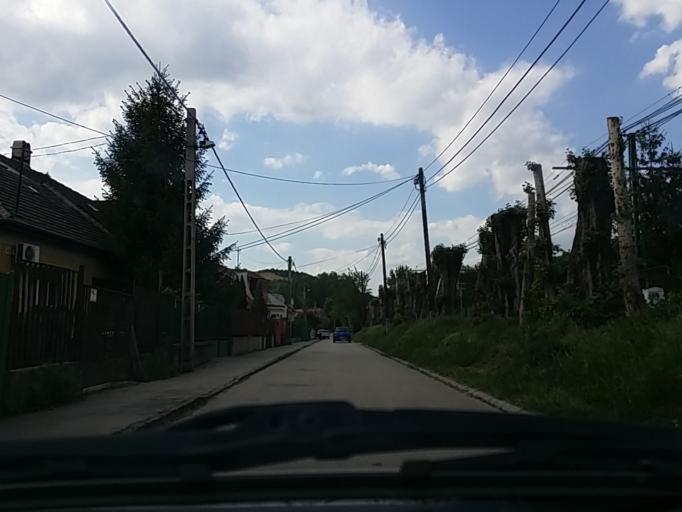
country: HU
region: Pest
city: Urom
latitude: 47.5818
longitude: 19.0460
